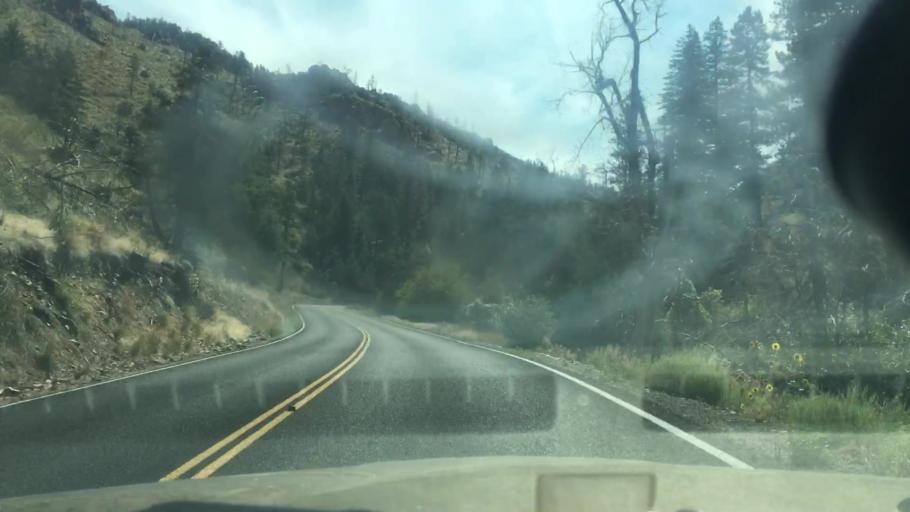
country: US
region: Colorado
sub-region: Larimer County
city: Laporte
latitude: 40.6718
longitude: -105.3853
